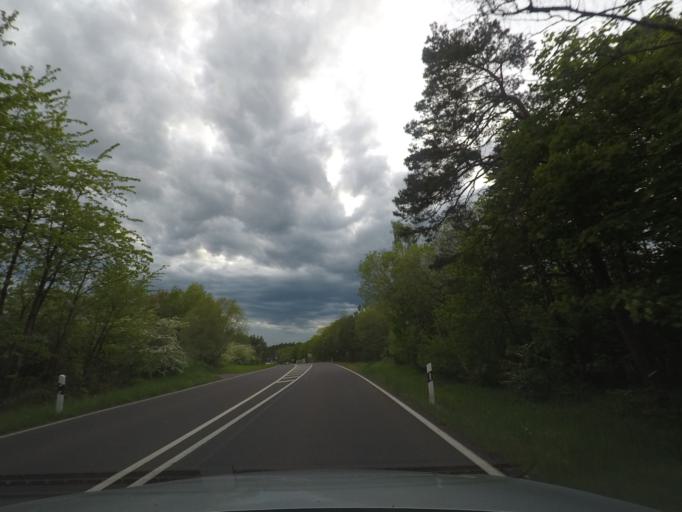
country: DE
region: Saxony-Anhalt
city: Beendorf
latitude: 52.2200
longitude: 11.0777
